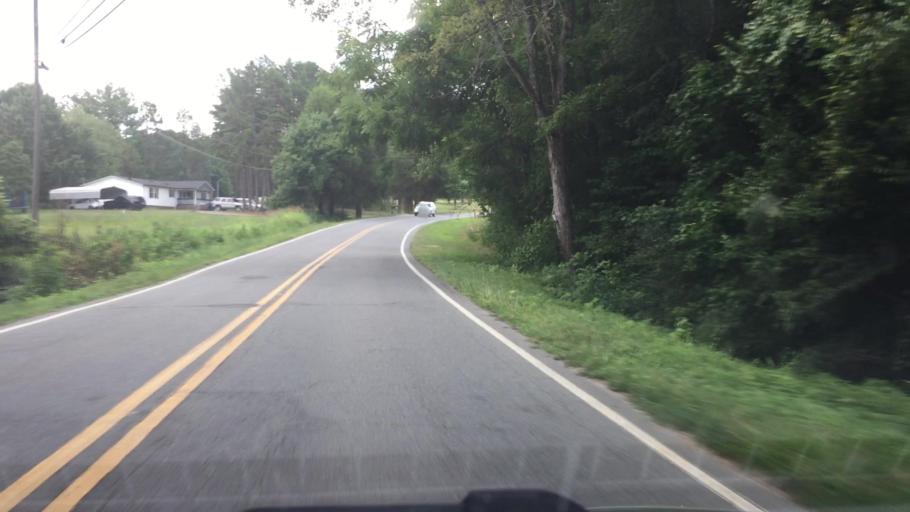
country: US
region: North Carolina
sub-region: Rowan County
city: Enochville
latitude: 35.4672
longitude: -80.7300
